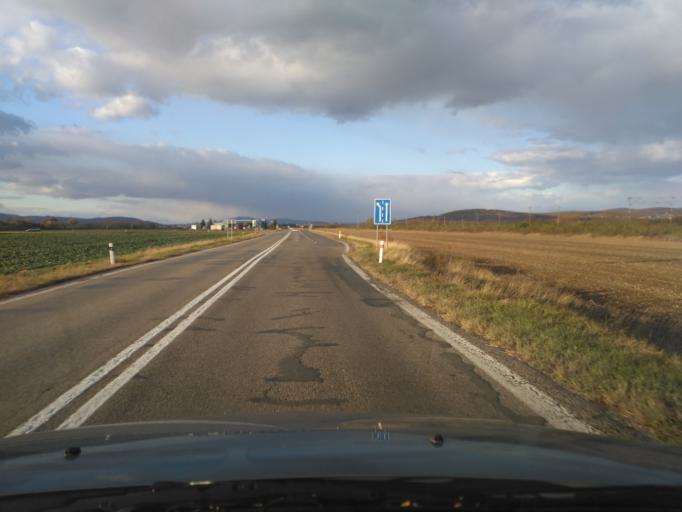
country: HU
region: Borsod-Abauj-Zemplen
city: Satoraljaujhely
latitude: 48.4246
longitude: 21.6611
